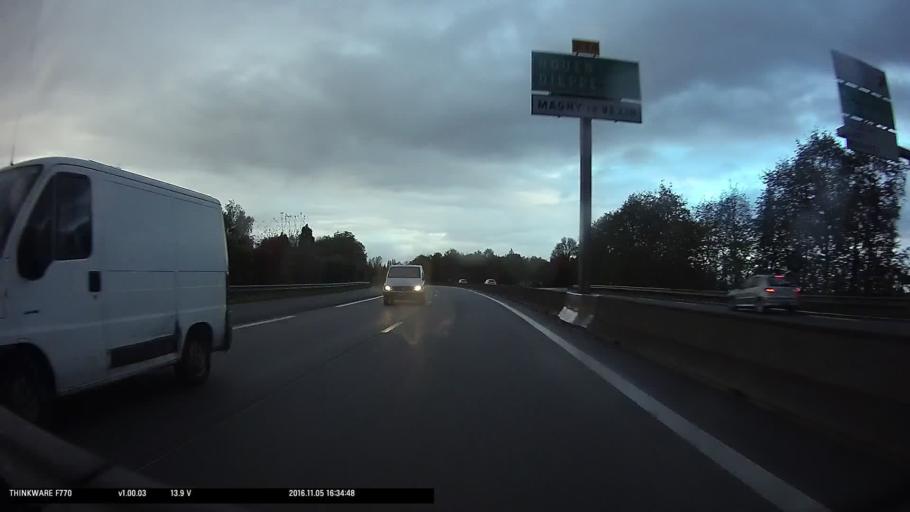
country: FR
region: Ile-de-France
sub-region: Departement du Val-d'Oise
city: Ableiges
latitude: 49.0700
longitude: 1.9689
